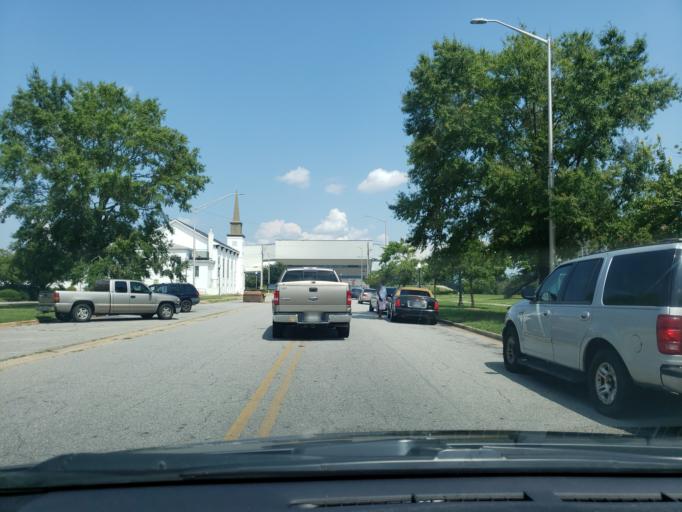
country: US
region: Georgia
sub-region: Dougherty County
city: Albany
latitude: 31.5738
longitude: -84.1528
